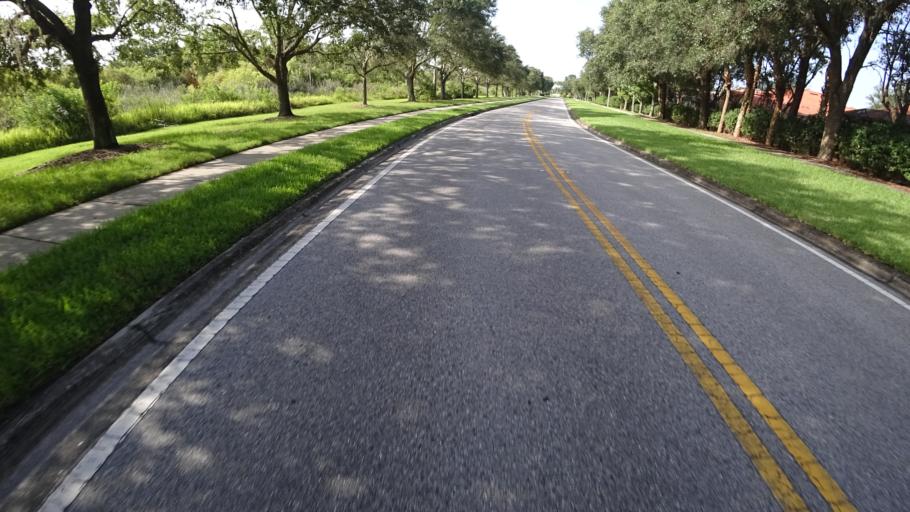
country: US
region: Florida
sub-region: Sarasota County
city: Desoto Lakes
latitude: 27.4308
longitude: -82.4685
